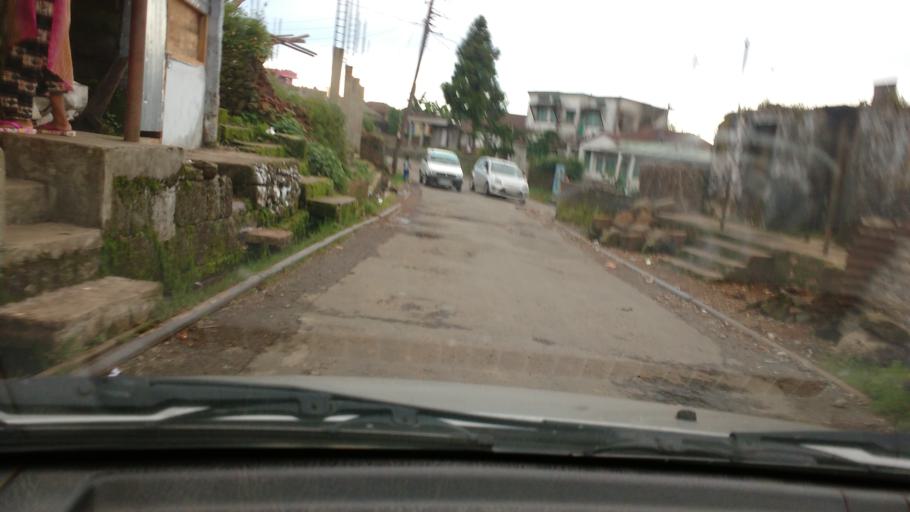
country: IN
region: Meghalaya
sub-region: East Khasi Hills
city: Cherrapunji
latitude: 25.2853
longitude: 91.7184
